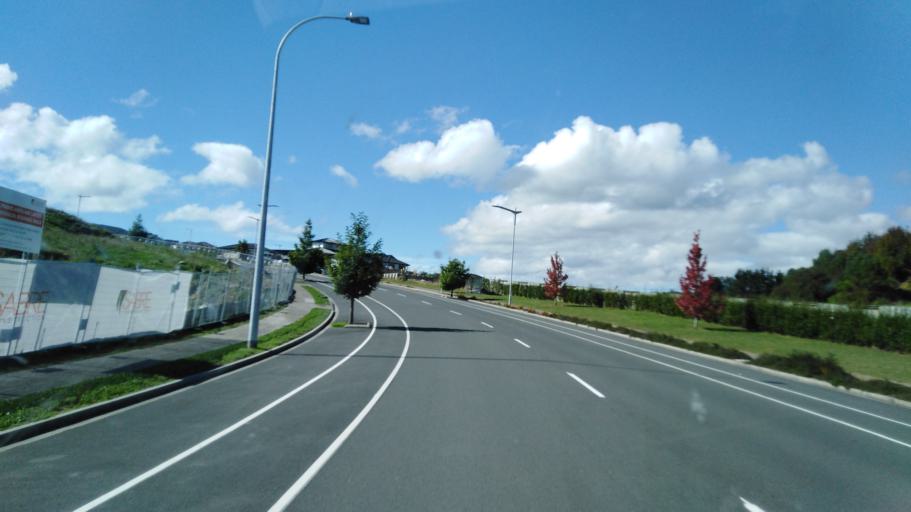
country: NZ
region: Bay of Plenty
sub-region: Tauranga City
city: Tauranga
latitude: -37.7619
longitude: 176.1051
